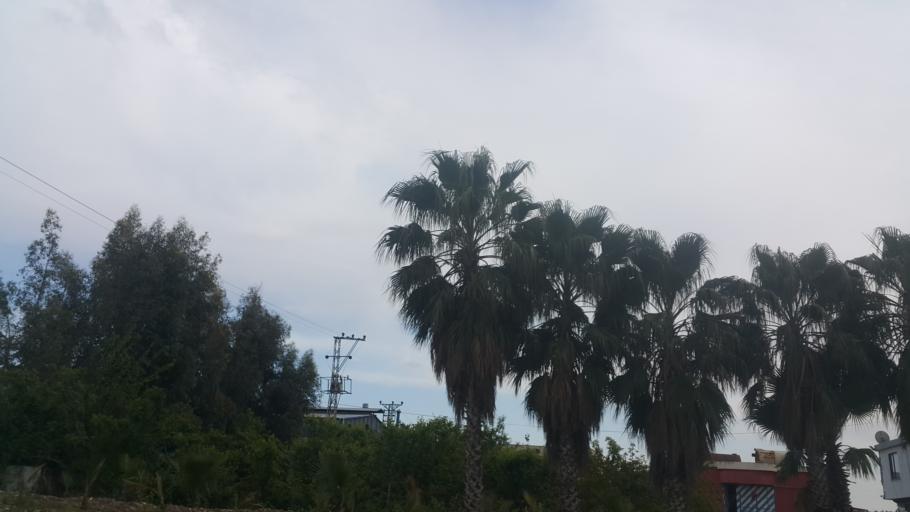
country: TR
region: Mersin
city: Yenice
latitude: 36.9766
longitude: 35.0714
